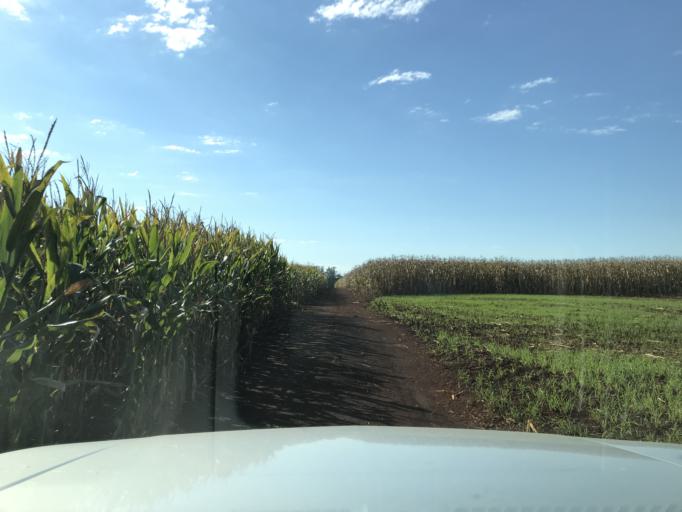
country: BR
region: Parana
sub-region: Palotina
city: Palotina
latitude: -24.2639
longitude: -53.8101
